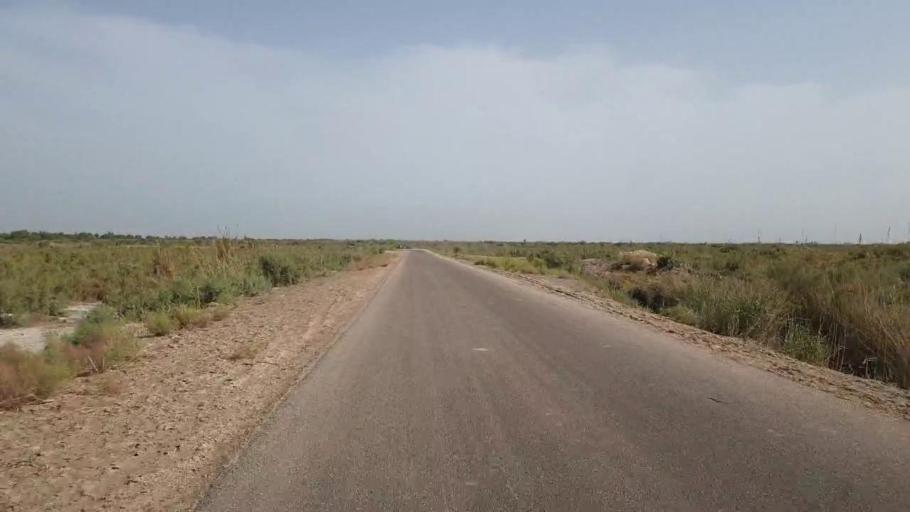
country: PK
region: Sindh
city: Sakrand
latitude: 26.2752
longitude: 68.2717
